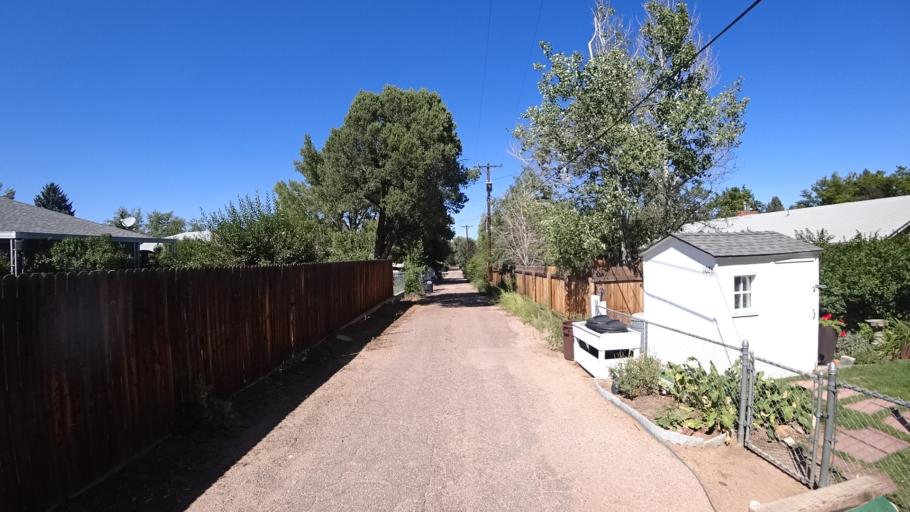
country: US
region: Colorado
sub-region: El Paso County
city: Colorado Springs
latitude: 38.8481
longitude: -104.7976
